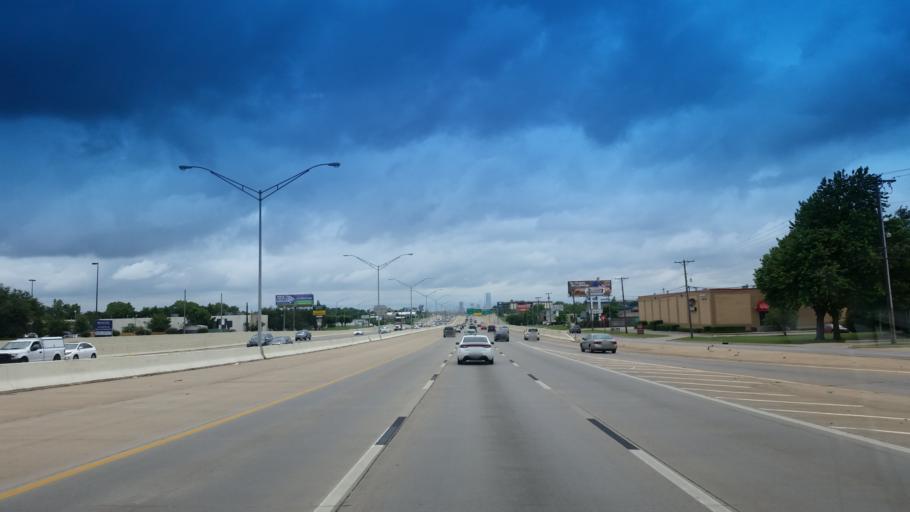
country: US
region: Oklahoma
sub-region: Oklahoma County
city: Nichols Hills
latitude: 35.5488
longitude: -97.5141
